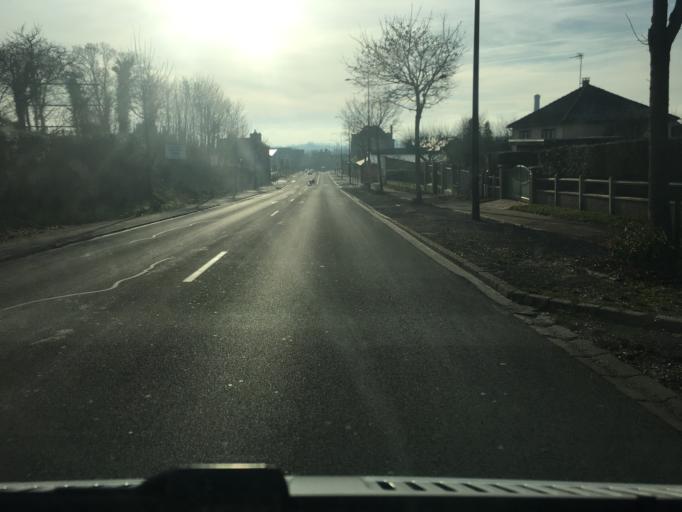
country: FR
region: Picardie
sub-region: Departement de la Somme
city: Abbeville
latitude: 50.1200
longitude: 1.8295
